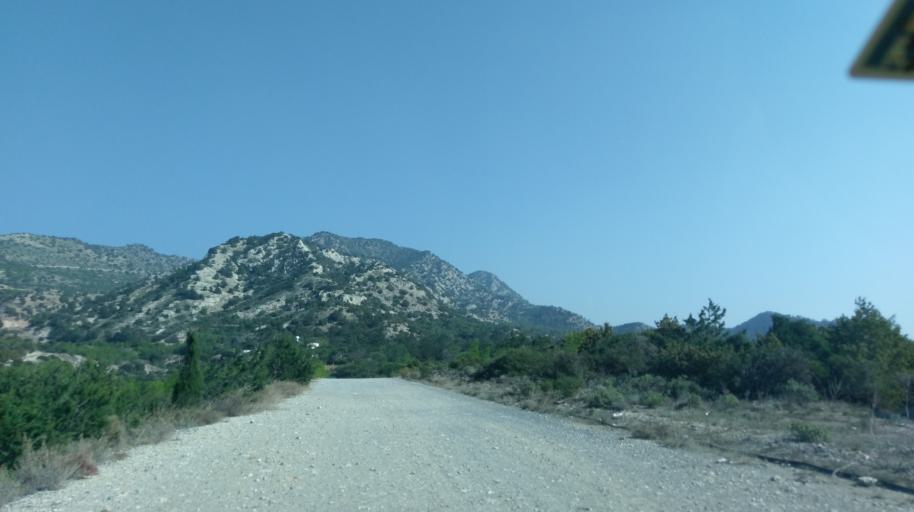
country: CY
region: Ammochostos
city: Lefkonoiko
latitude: 35.3410
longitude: 33.7205
